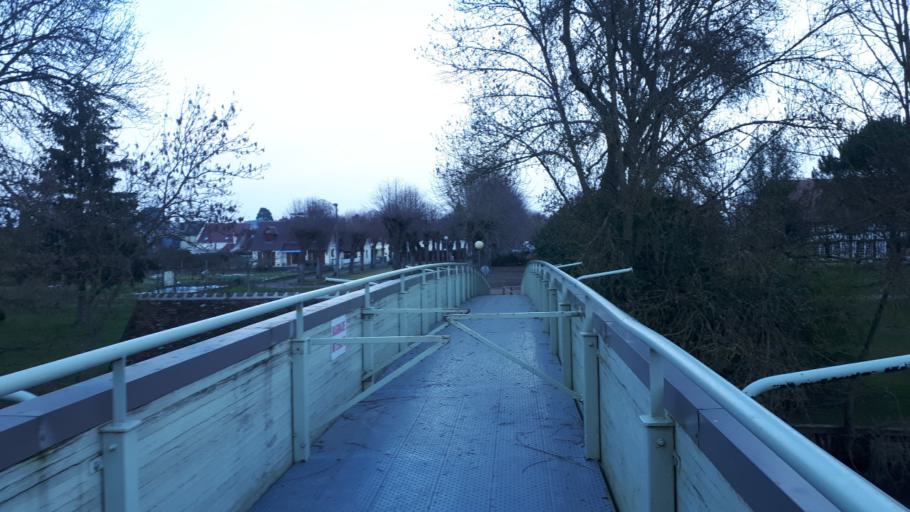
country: FR
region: Centre
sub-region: Departement du Loir-et-Cher
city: Montoire-sur-le-Loir
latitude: 47.7494
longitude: 0.8625
